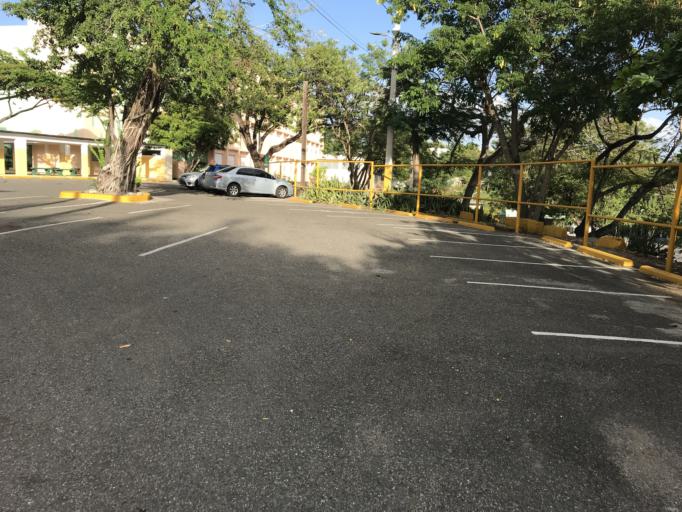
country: DO
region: Nacional
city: La Julia
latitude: 18.4623
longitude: -69.9228
